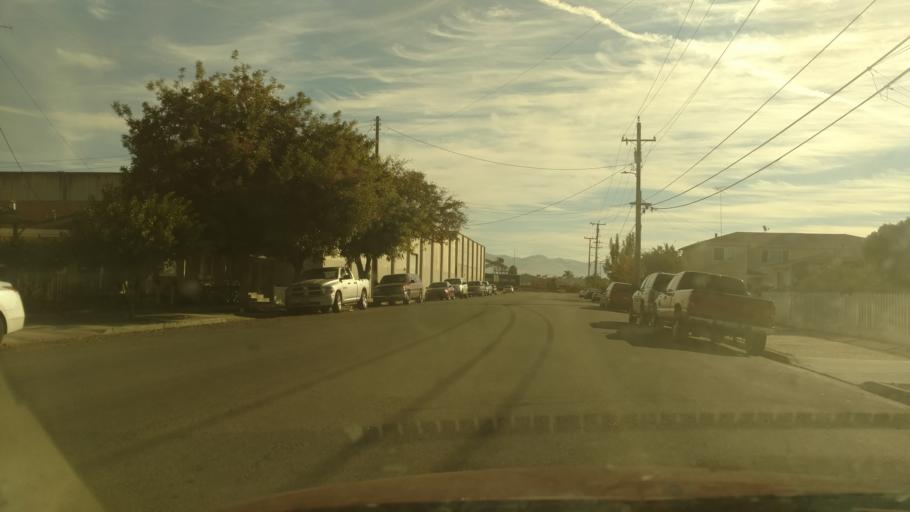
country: US
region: California
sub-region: San Benito County
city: Hollister
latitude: 36.8463
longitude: -121.3977
